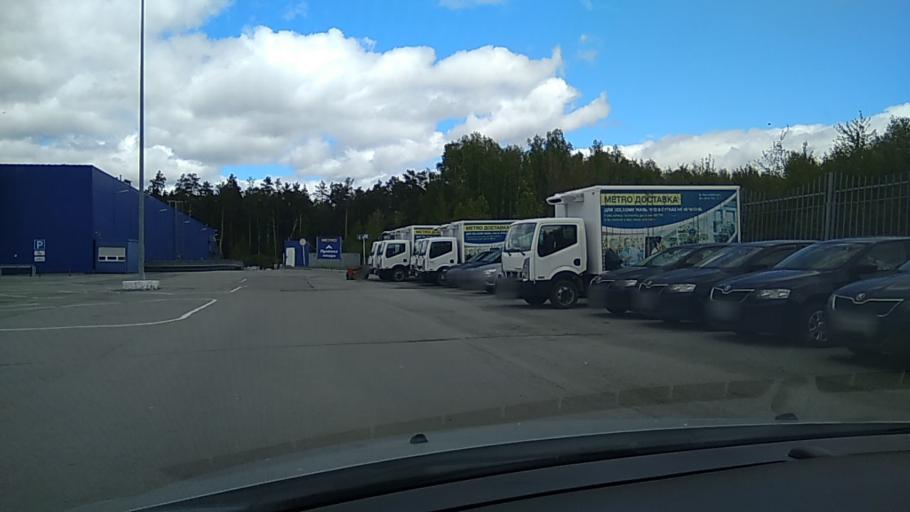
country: RU
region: Sverdlovsk
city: Istok
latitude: 56.8225
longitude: 60.7136
